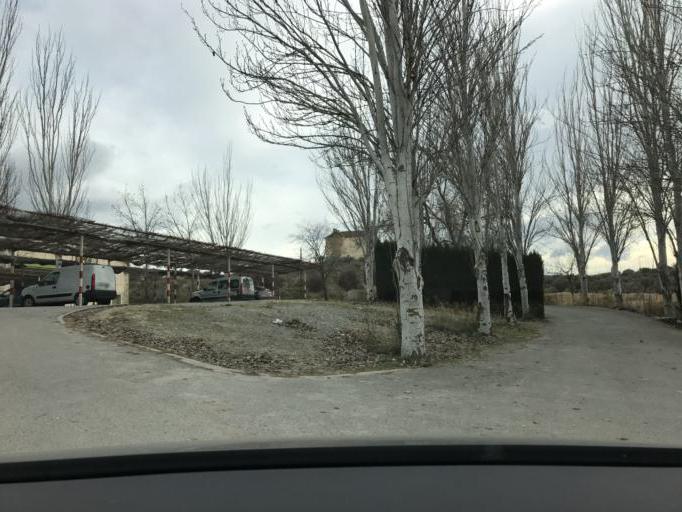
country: ES
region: Andalusia
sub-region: Provincia de Granada
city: Alhendin
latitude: 37.1154
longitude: -3.6644
